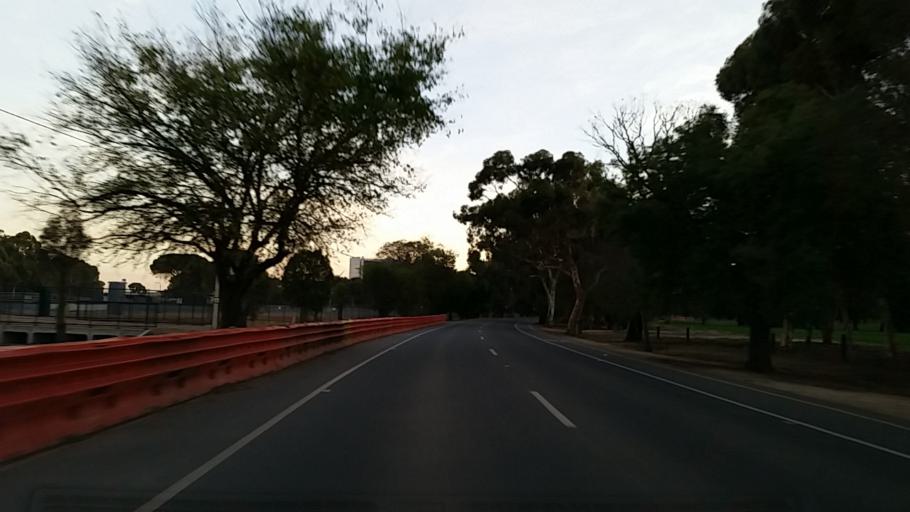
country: AU
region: South Australia
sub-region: Adelaide
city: North Adelaide
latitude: -34.9111
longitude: 138.5819
